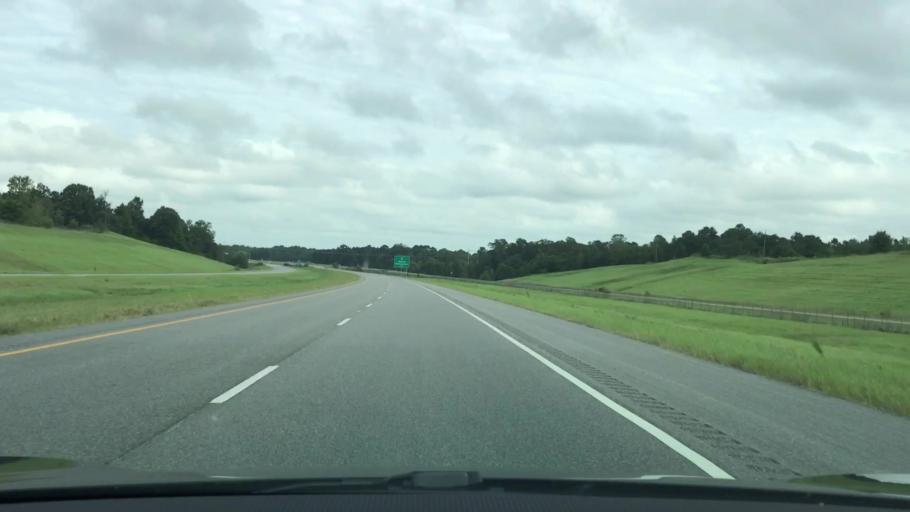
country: US
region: Alabama
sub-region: Montgomery County
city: Pike Road
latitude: 32.3502
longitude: -86.0651
